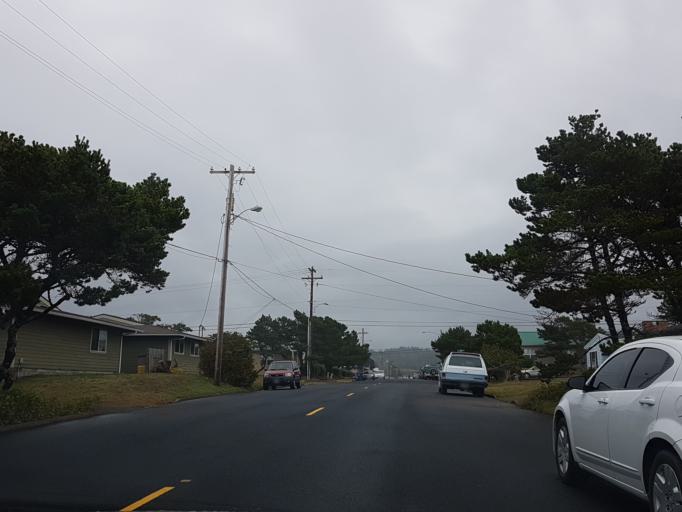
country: US
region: Oregon
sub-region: Lincoln County
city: Newport
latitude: 44.6447
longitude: -124.0578
